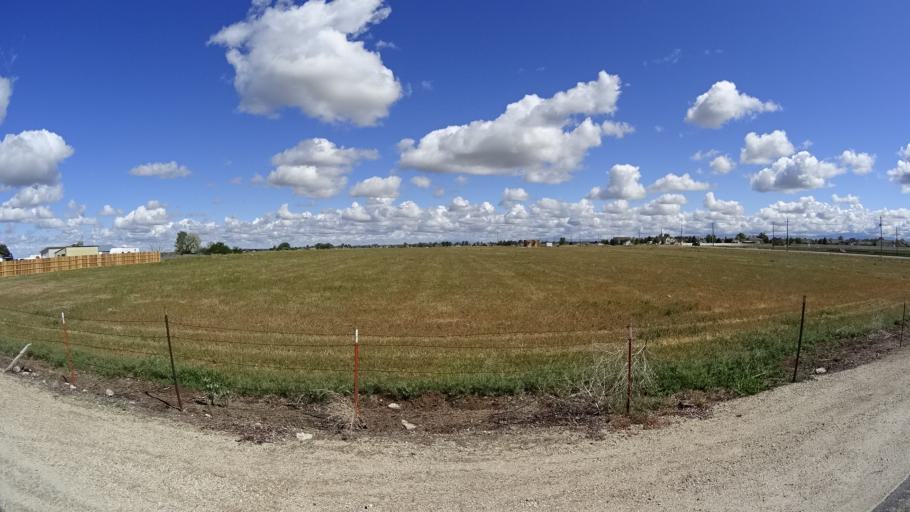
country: US
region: Idaho
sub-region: Ada County
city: Kuna
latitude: 43.5102
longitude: -116.4352
